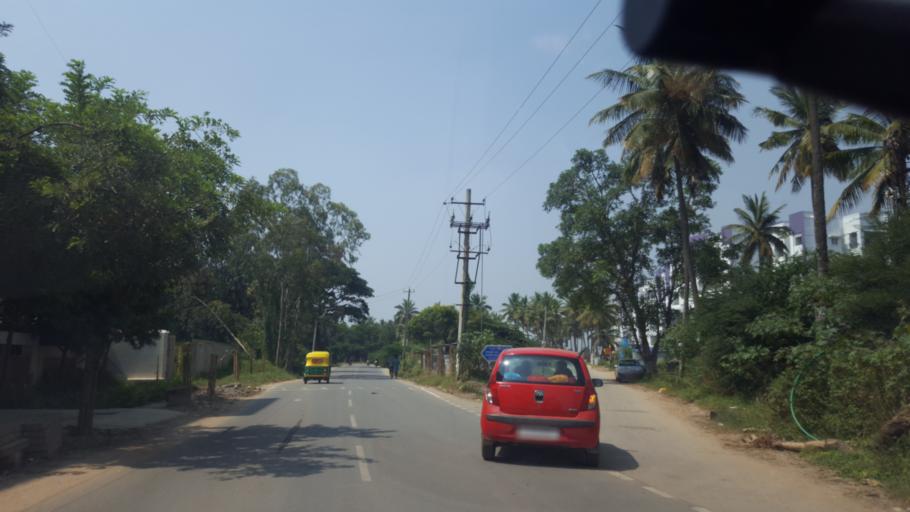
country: IN
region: Karnataka
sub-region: Bangalore Urban
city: Bangalore
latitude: 12.9379
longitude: 77.7127
